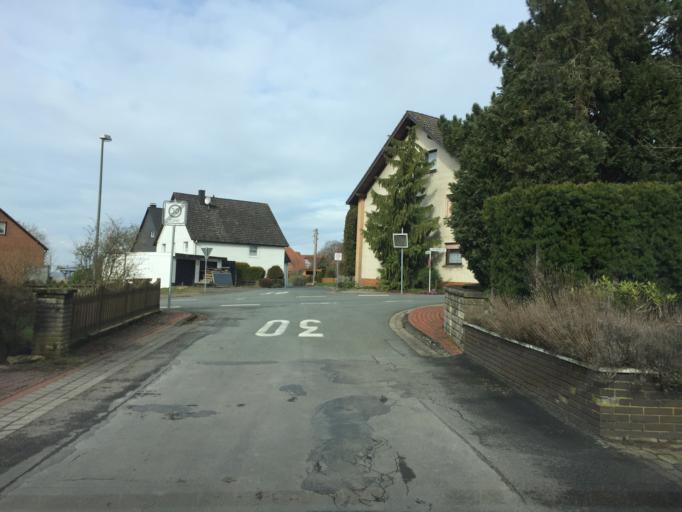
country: DE
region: Lower Saxony
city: Rinteln
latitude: 52.1042
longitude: 9.1542
